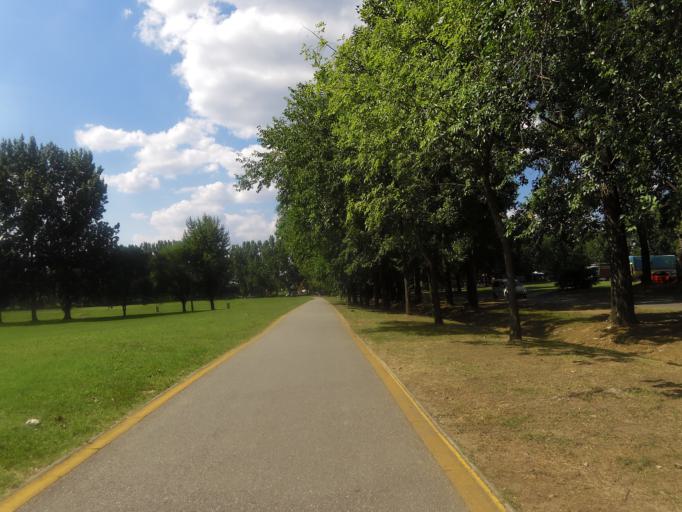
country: HU
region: Jasz-Nagykun-Szolnok
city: Tiszafured
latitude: 47.6231
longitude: 20.7373
